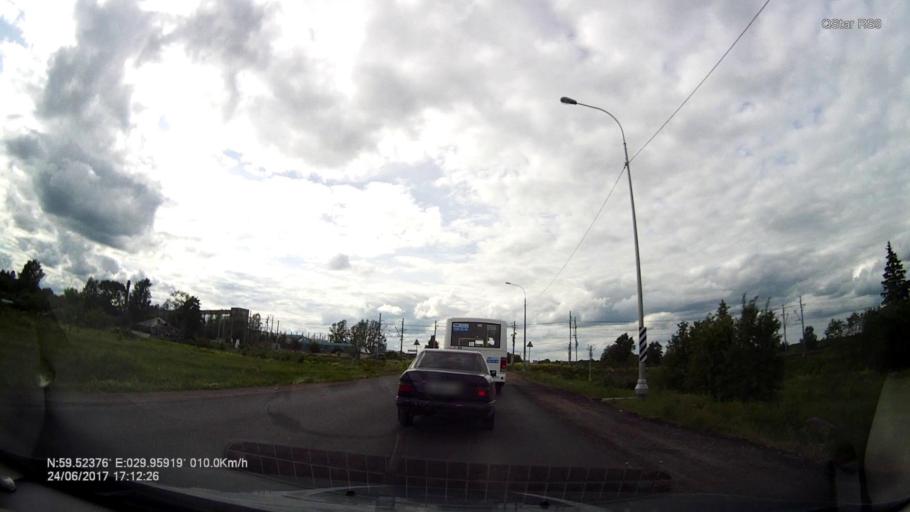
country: RU
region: Leningrad
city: Voyskovitsy
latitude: 59.5238
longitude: 29.9591
